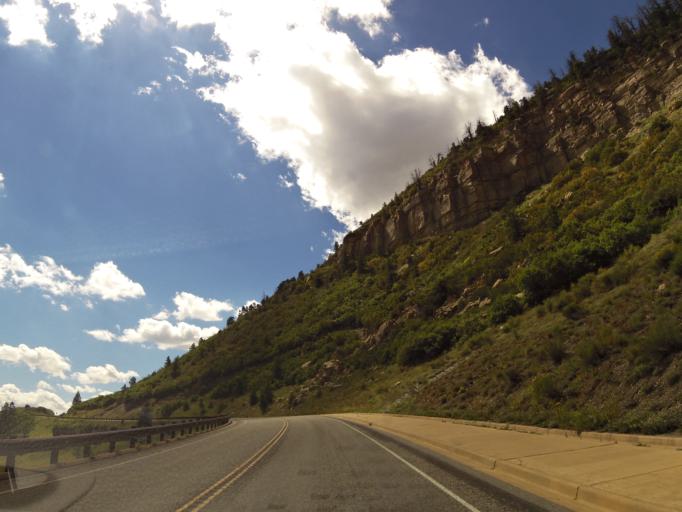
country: US
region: Colorado
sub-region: Montezuma County
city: Mancos
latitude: 37.3067
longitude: -108.4130
